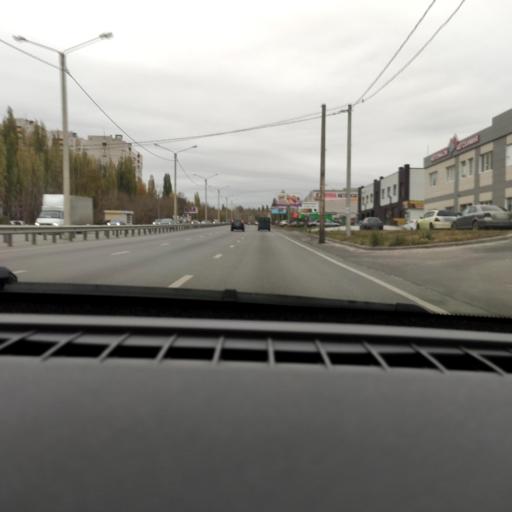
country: RU
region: Voronezj
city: Voronezh
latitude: 51.6595
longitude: 39.1323
